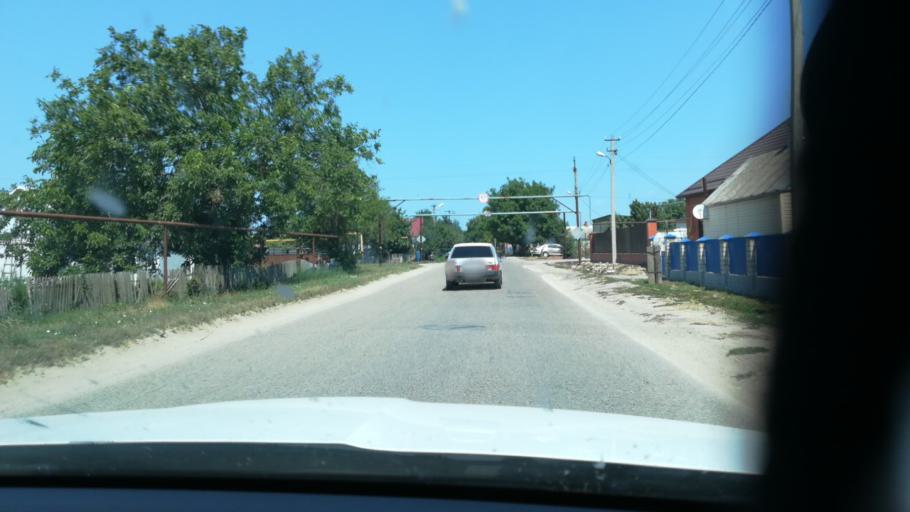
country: RU
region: Krasnodarskiy
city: Starotitarovskaya
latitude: 45.2131
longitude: 37.1441
